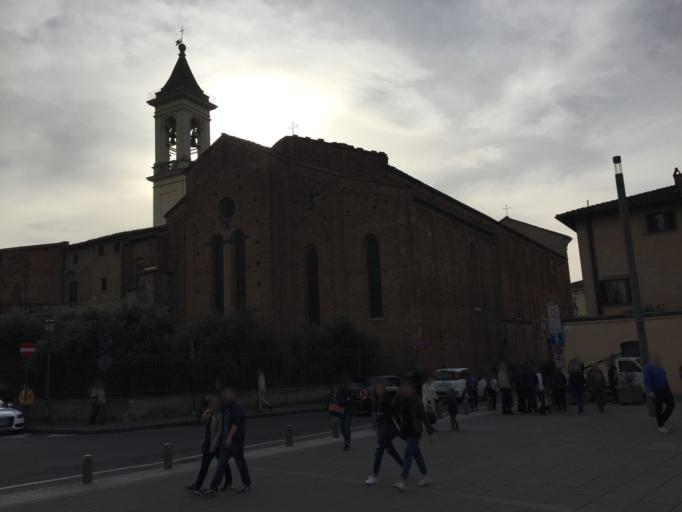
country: IT
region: Tuscany
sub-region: Provincia di Prato
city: Prato
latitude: 43.8791
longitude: 11.0979
